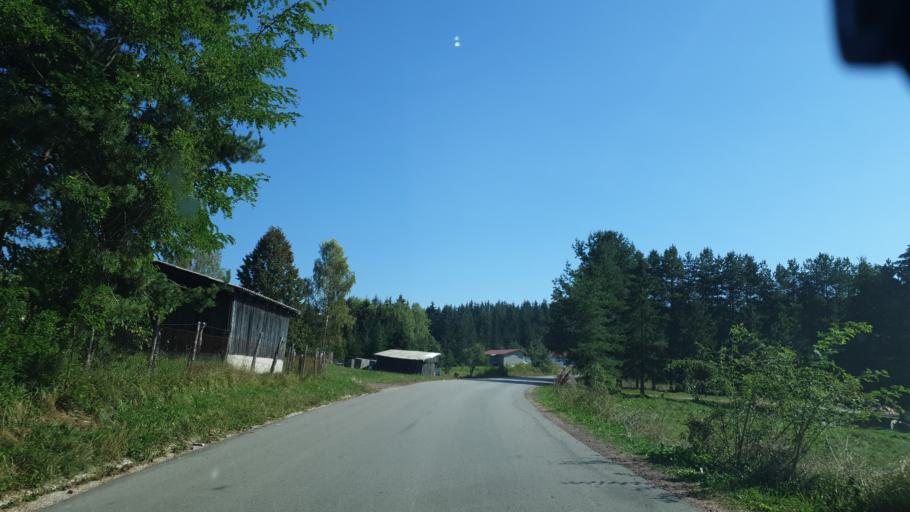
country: RS
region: Central Serbia
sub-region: Zlatiborski Okrug
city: Nova Varos
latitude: 43.4293
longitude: 19.8825
